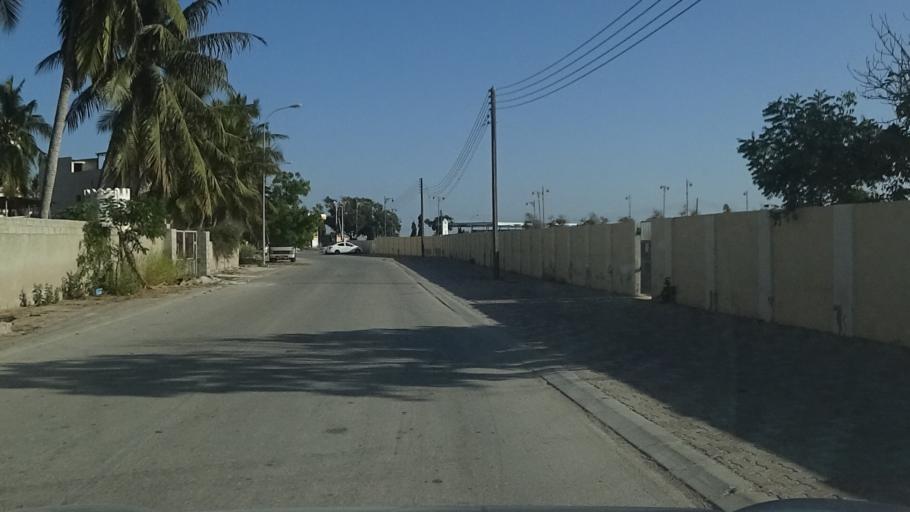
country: OM
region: Zufar
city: Salalah
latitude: 17.0277
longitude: 54.1702
